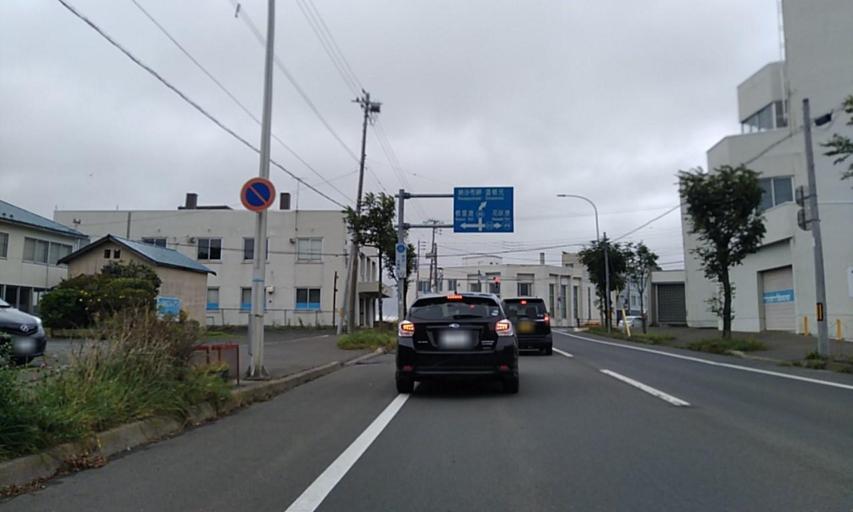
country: JP
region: Hokkaido
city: Nemuro
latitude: 43.3367
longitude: 145.5794
